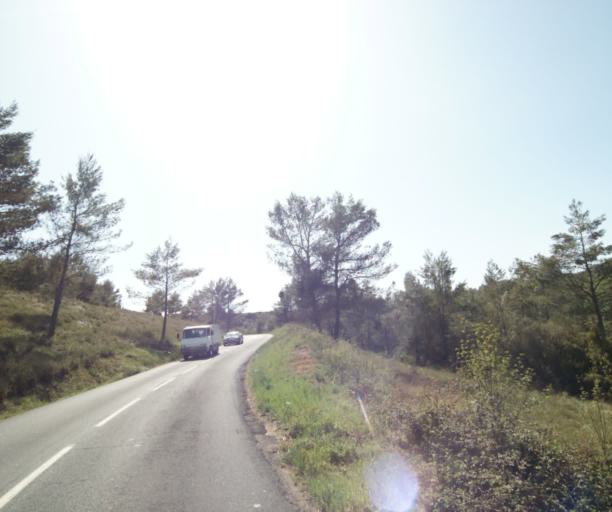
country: FR
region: Languedoc-Roussillon
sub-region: Departement de l'Herault
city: Grabels
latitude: 43.6474
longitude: 3.7771
